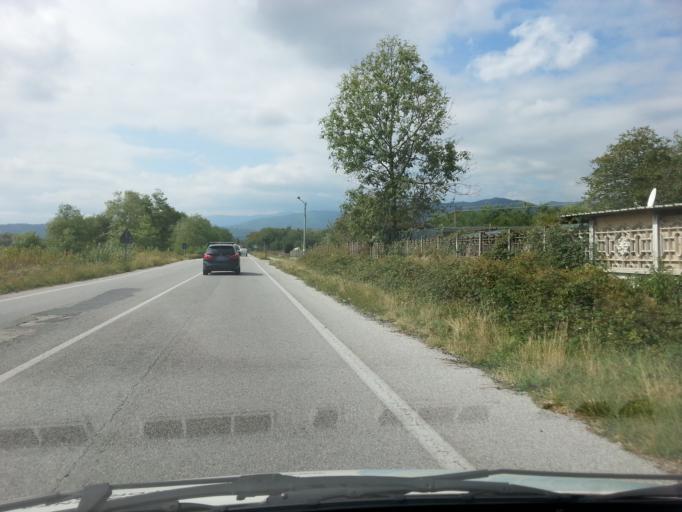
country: IT
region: Piedmont
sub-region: Provincia di Torino
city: Frossasco
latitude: 44.9439
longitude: 7.3808
